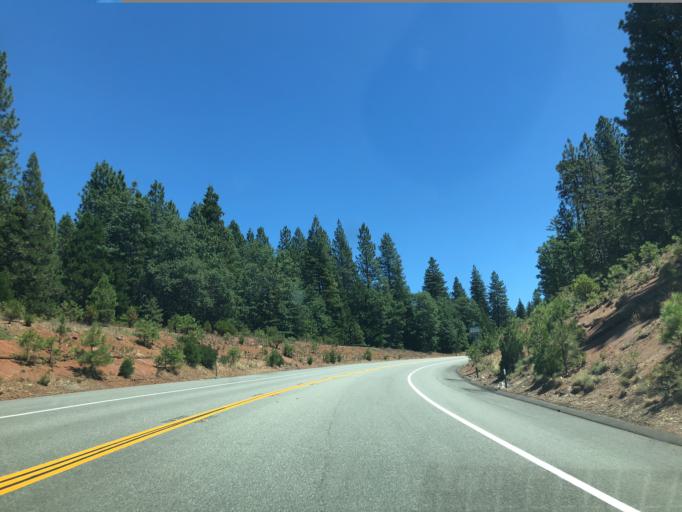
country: US
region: California
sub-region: Shasta County
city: Shingletown
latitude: 40.4951
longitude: -121.9078
